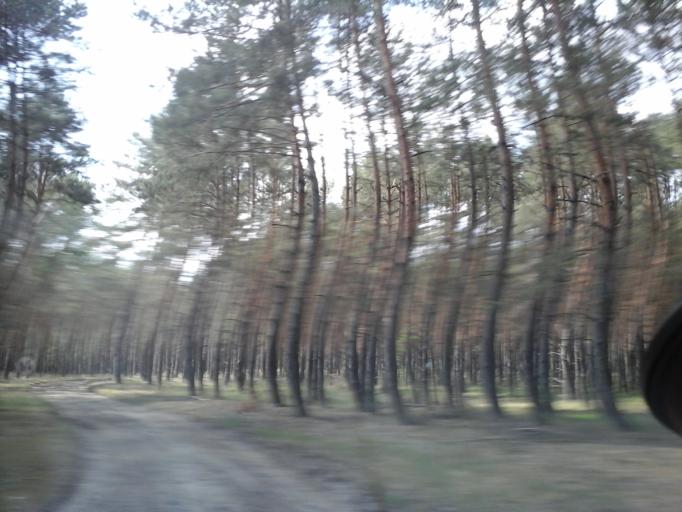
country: PL
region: West Pomeranian Voivodeship
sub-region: Powiat choszczenski
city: Drawno
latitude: 53.1133
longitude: 15.7716
